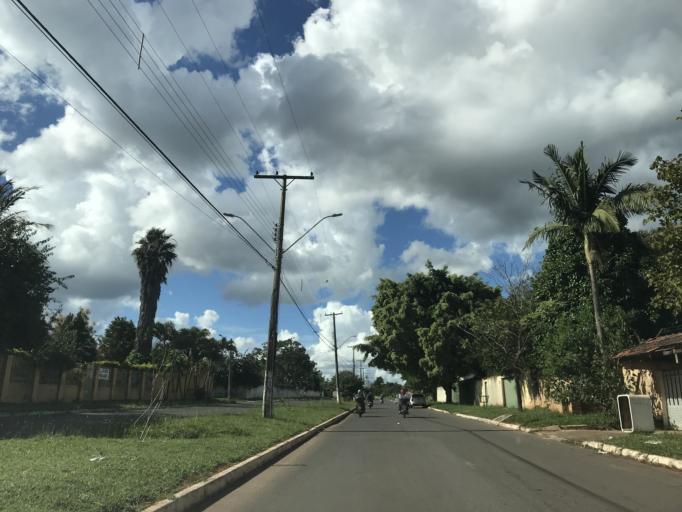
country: BR
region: Federal District
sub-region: Brasilia
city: Brasilia
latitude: -15.7508
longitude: -47.7519
